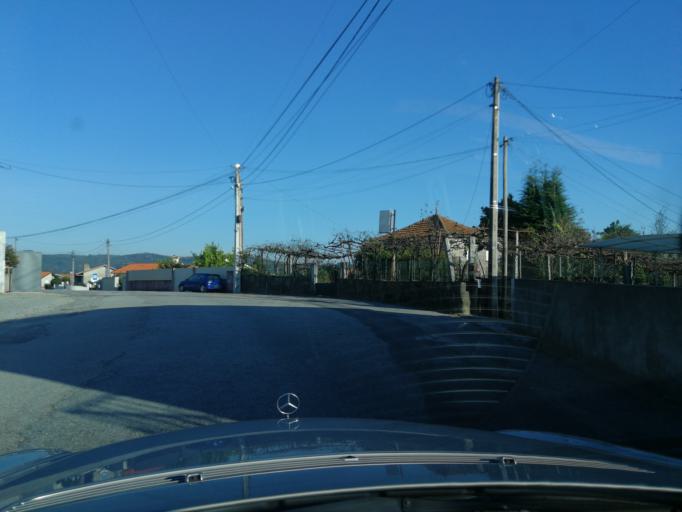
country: PT
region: Braga
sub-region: Vila Nova de Famalicao
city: Vila Nova de Famalicao
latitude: 41.4298
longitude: -8.5083
